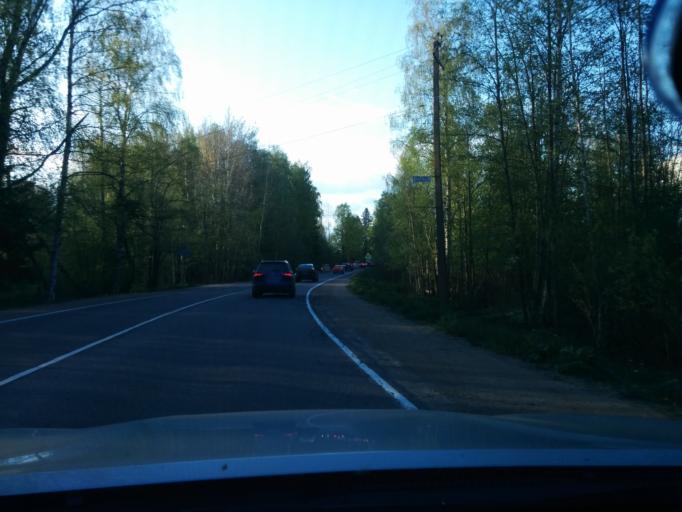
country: RU
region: Leningrad
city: Verkhniye Osel'ki
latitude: 60.2298
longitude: 30.4320
